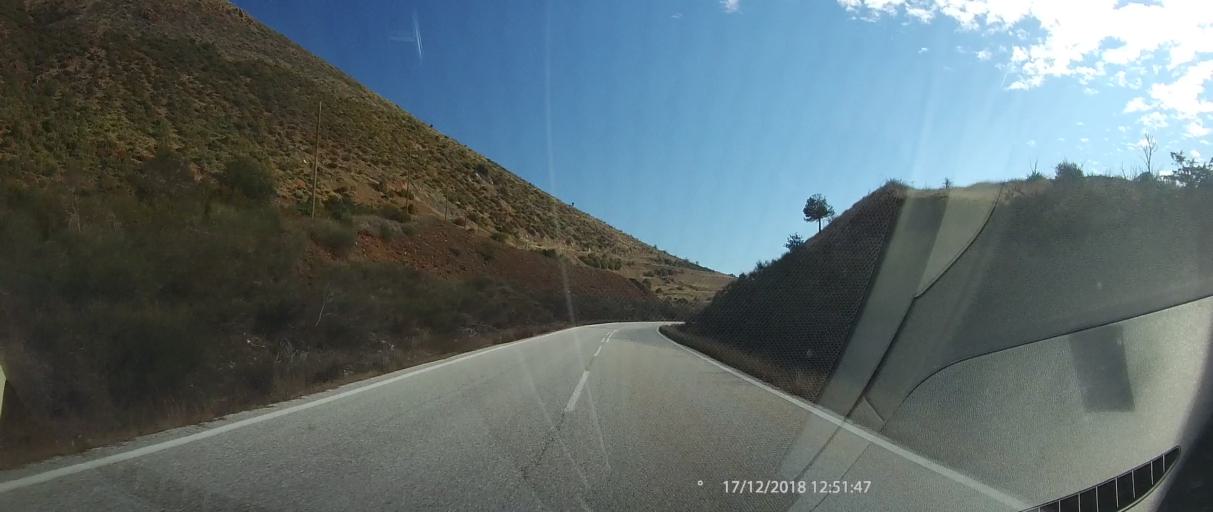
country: GR
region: Thessaly
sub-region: Trikala
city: Kastraki
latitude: 39.7631
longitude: 21.4710
